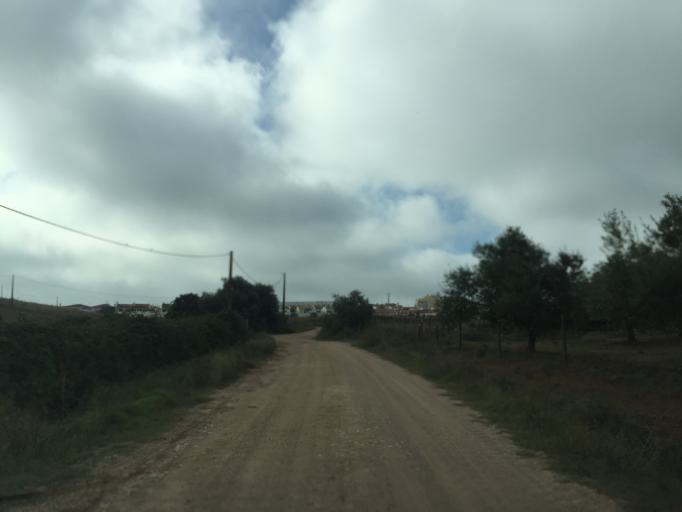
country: PT
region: Portalegre
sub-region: Fronteira
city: Fronteira
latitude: 39.0555
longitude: -7.6396
